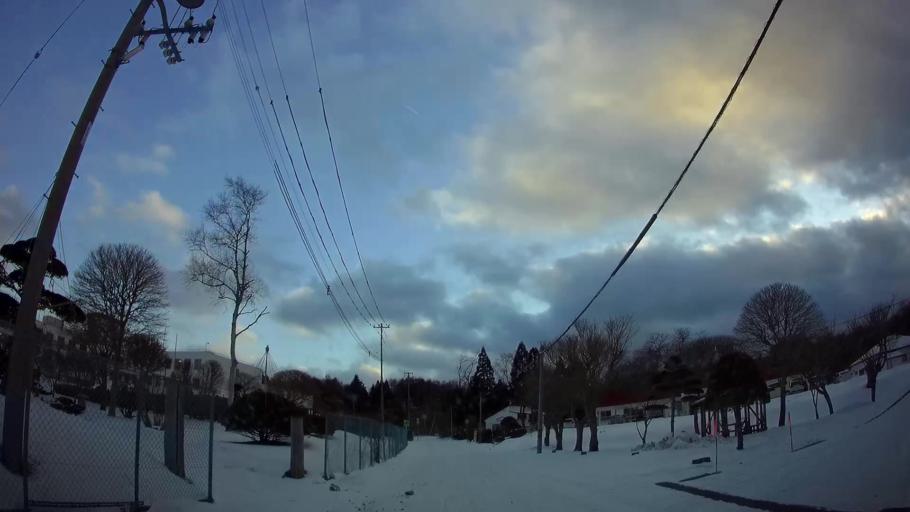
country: JP
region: Hokkaido
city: Nanae
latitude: 42.0238
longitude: 140.8329
